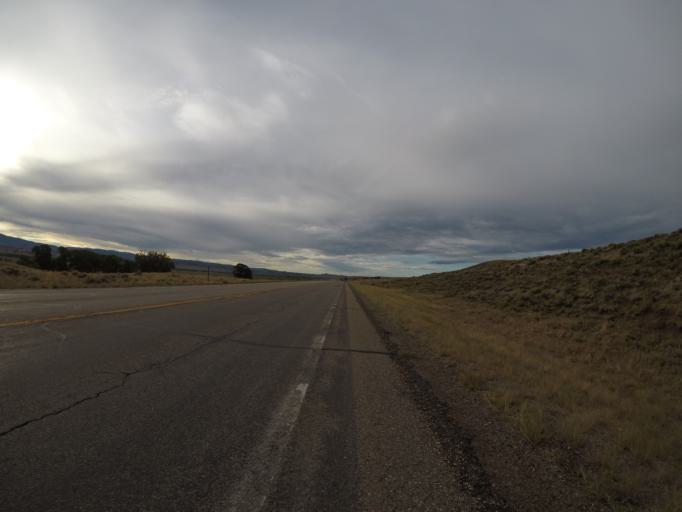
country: US
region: Wyoming
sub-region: Carbon County
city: Saratoga
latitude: 41.4054
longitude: -106.7752
